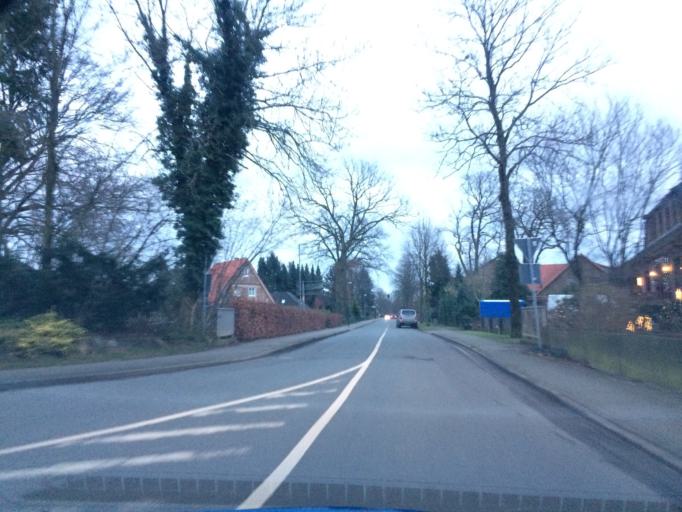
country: DE
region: Lower Saxony
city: Radbruch
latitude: 53.3106
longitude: 10.2850
